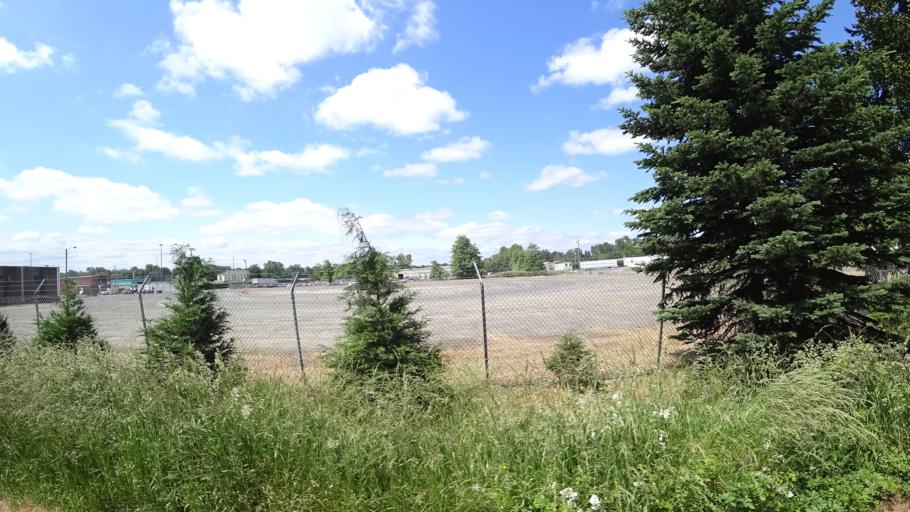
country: US
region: Washington
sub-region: Clark County
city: Vancouver
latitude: 45.5991
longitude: -122.6641
